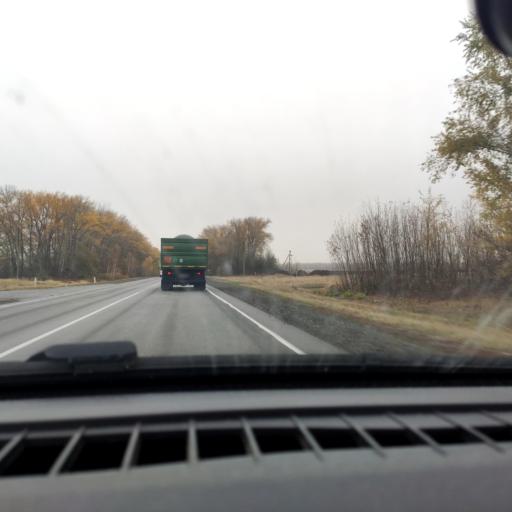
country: RU
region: Voronezj
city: Ostrogozhsk
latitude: 50.9661
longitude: 39.0122
